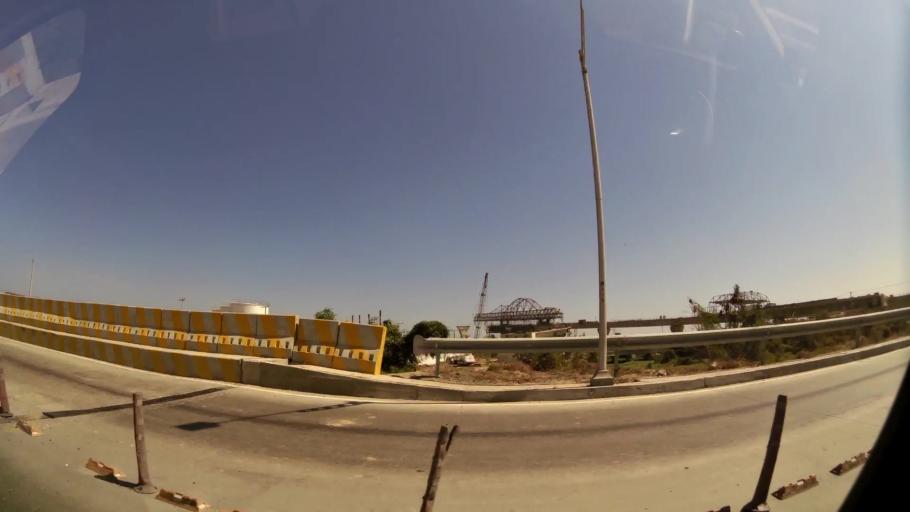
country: CO
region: Atlantico
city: Barranquilla
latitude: 10.9529
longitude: -74.7655
